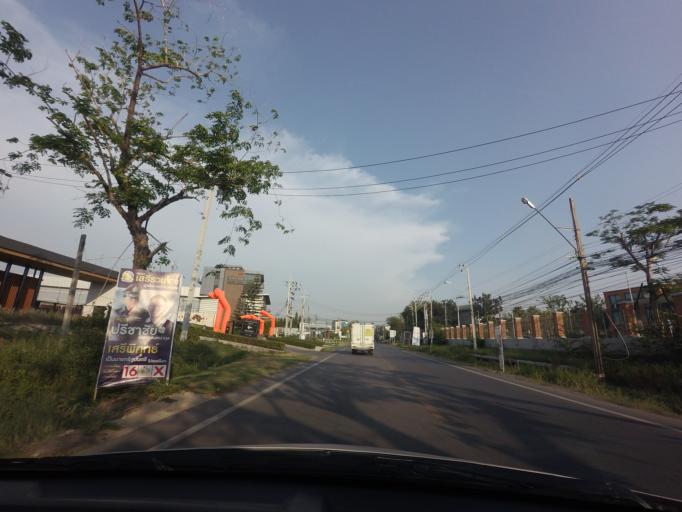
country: TH
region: Bangkok
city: Suan Luang
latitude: 13.7442
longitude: 100.6720
